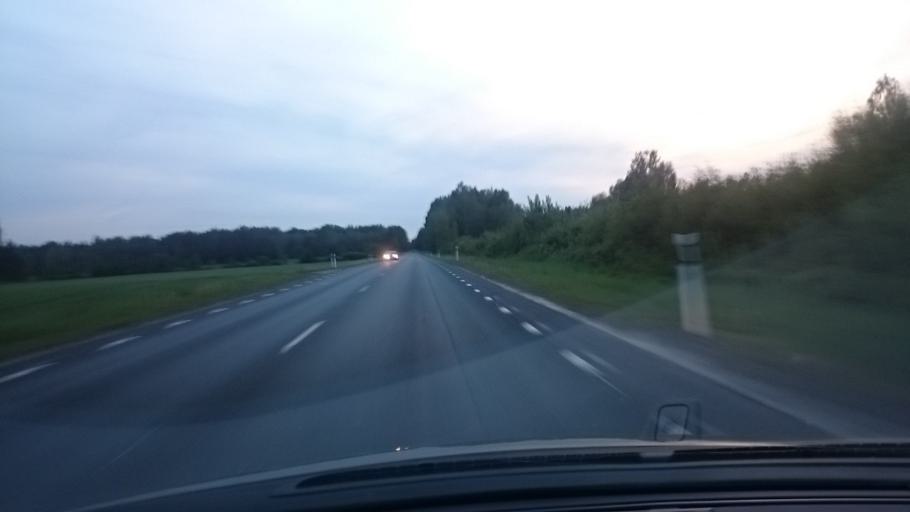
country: EE
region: Paernumaa
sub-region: Vaendra vald (alev)
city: Vandra
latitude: 58.8400
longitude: 25.0679
